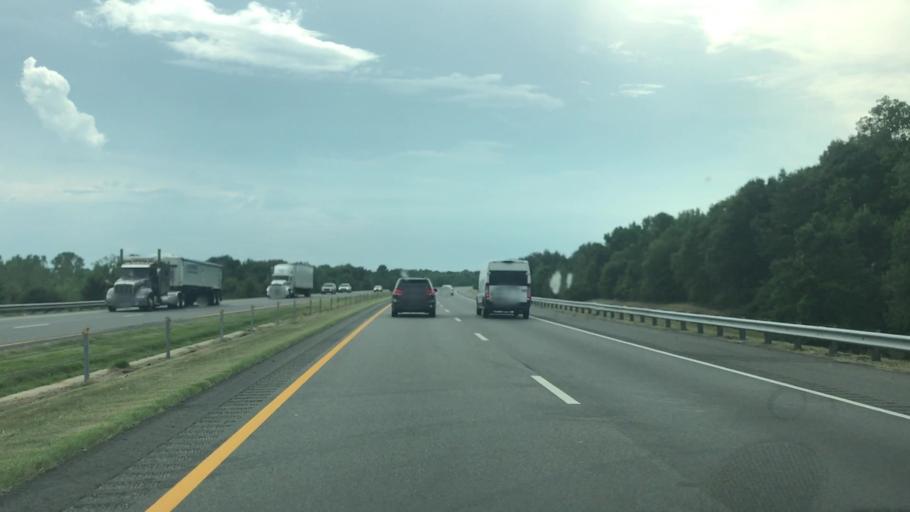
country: US
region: Arkansas
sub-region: Monroe County
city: Brinkley
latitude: 34.8766
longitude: -91.2713
